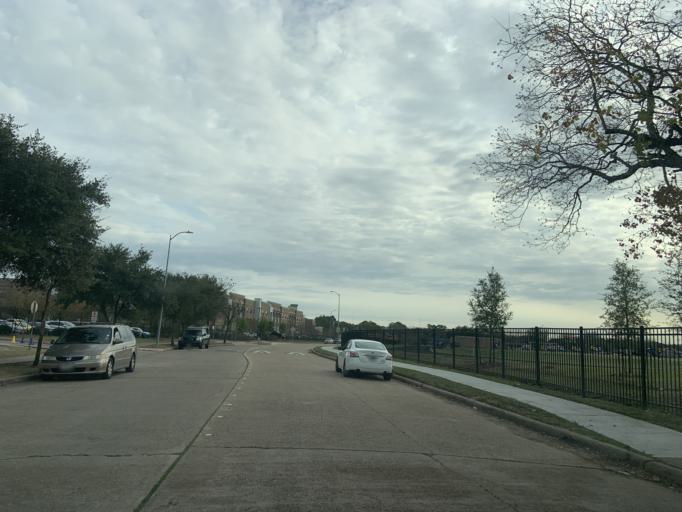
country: US
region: Texas
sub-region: Harris County
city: Bellaire
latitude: 29.6872
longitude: -95.5138
